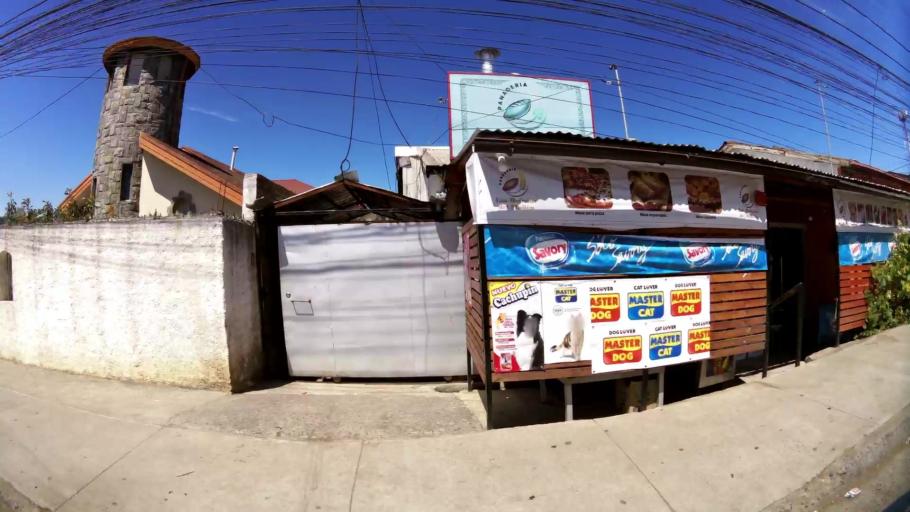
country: CL
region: Biobio
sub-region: Provincia de Concepcion
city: Penco
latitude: -36.7489
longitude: -72.9944
